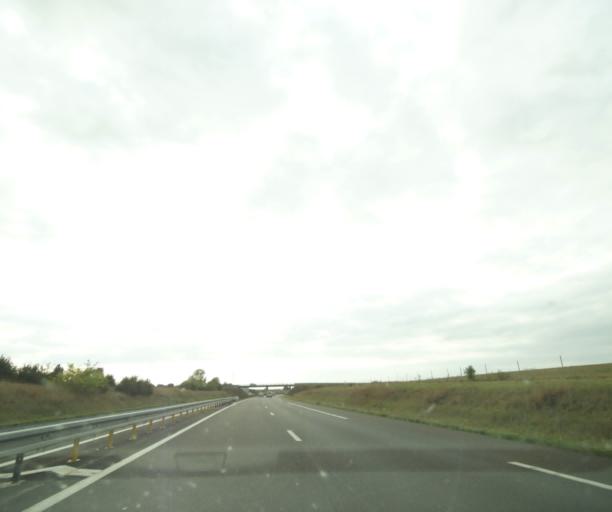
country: FR
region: Centre
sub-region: Departement d'Indre-et-Loire
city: Chanceaux-sur-Choisille
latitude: 47.4778
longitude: 0.6993
